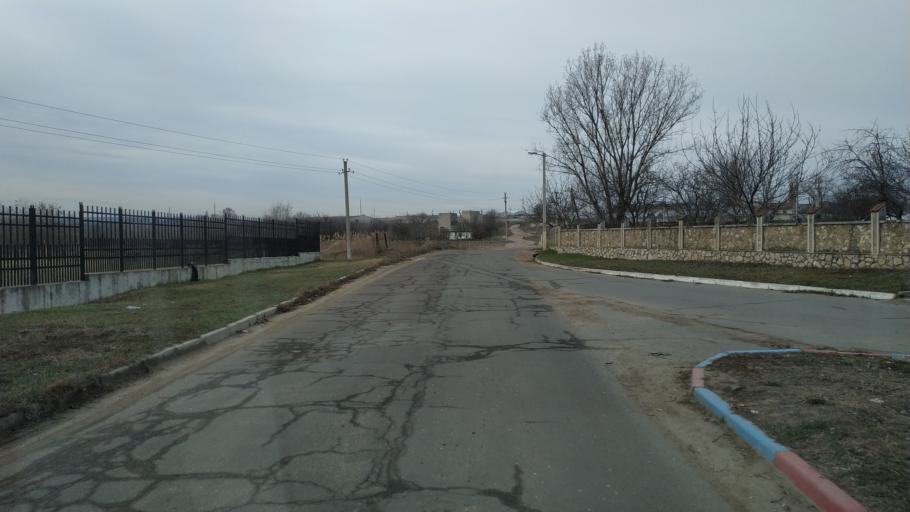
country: MD
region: Chisinau
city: Vatra
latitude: 47.0876
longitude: 28.7683
